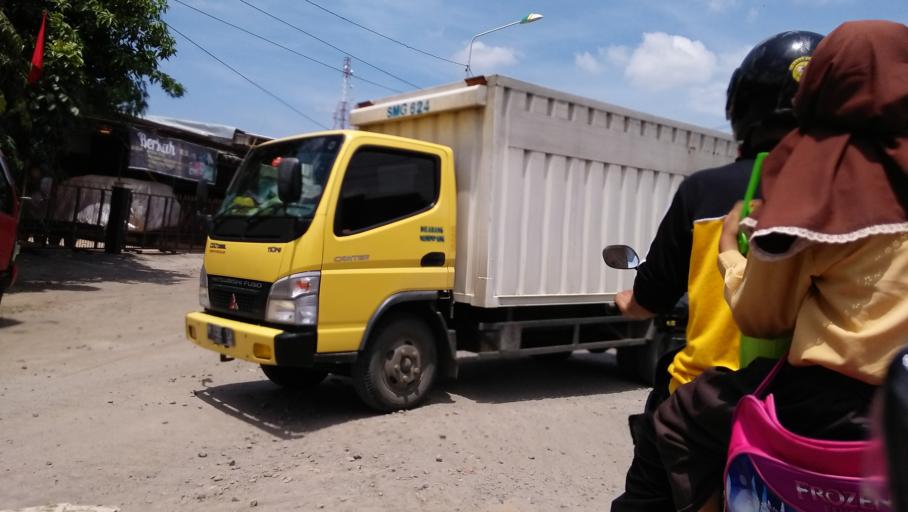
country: ID
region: Central Java
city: Semarang
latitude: -6.9863
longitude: 110.4745
